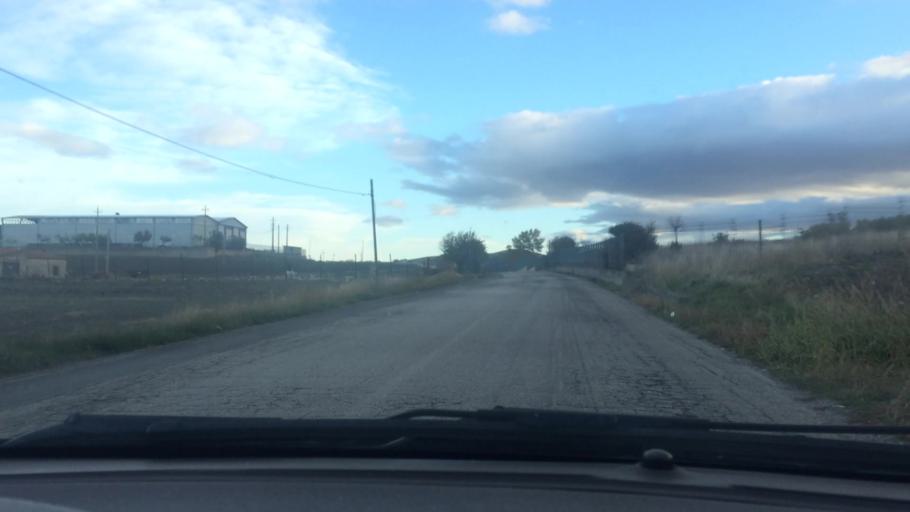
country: IT
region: Basilicate
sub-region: Provincia di Potenza
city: Tolve
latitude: 40.7095
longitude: 16.0184
